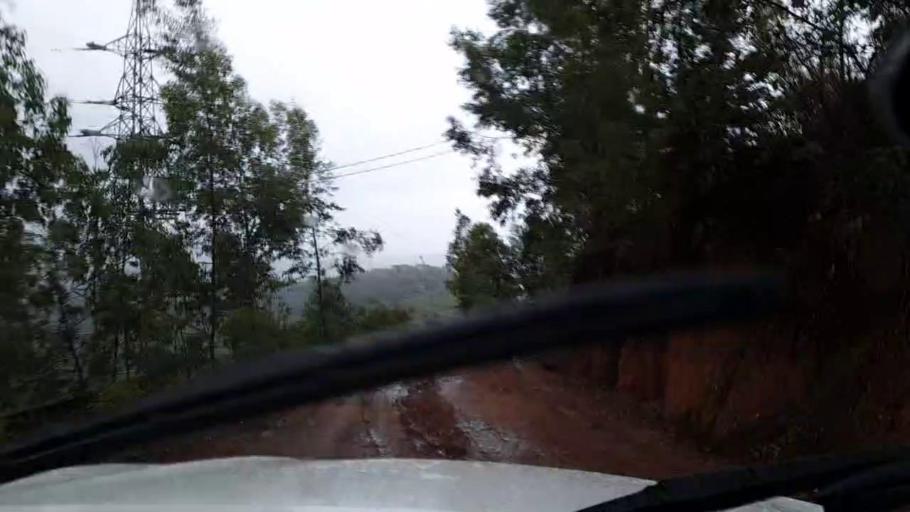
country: BI
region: Kayanza
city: Kayanza
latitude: -2.7829
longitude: 29.5332
